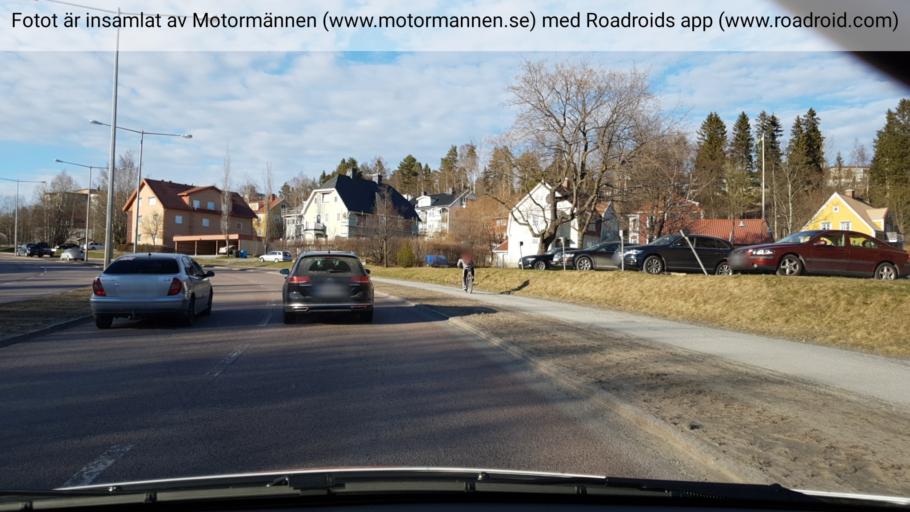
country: SE
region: Vaesternorrland
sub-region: OErnskoeldsviks Kommun
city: Ornskoldsvik
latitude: 63.2921
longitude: 18.7214
